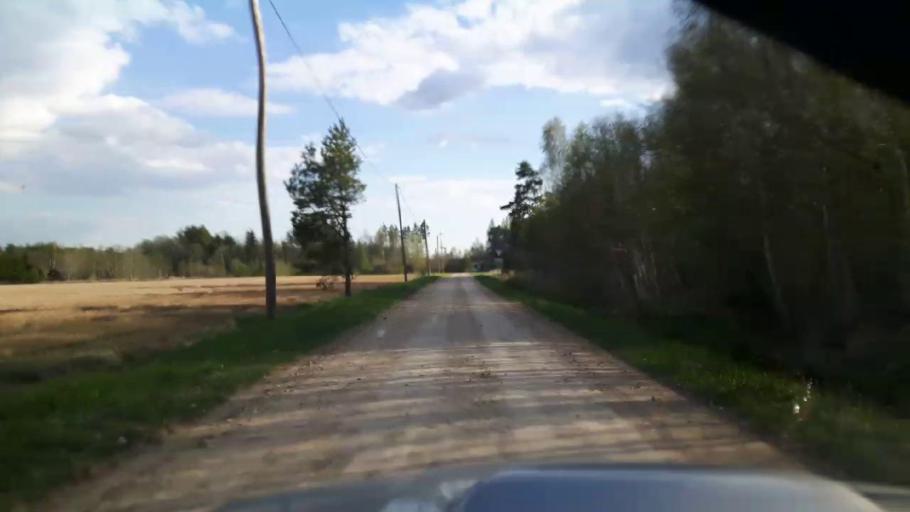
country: EE
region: Paernumaa
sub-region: Sindi linn
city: Sindi
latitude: 58.4323
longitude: 24.8059
